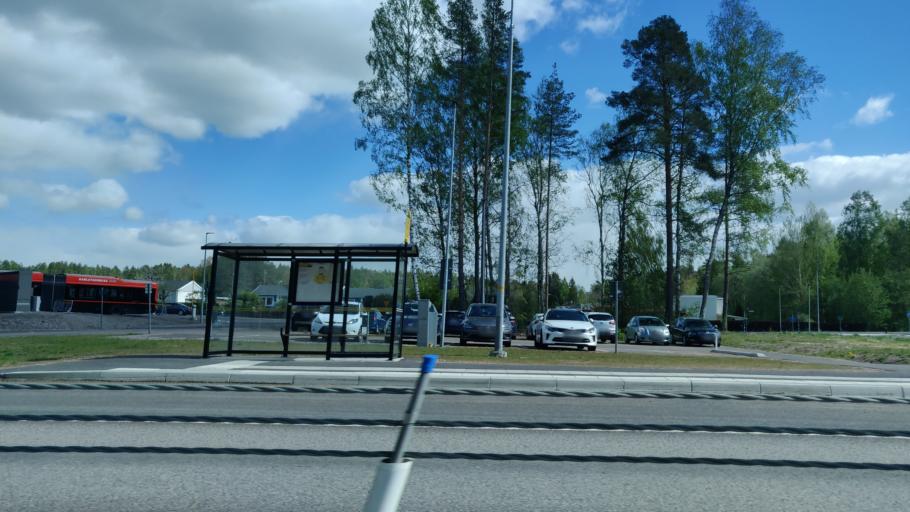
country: SE
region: Vaermland
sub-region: Karlstads Kommun
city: Karlstad
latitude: 59.4085
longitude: 13.5318
